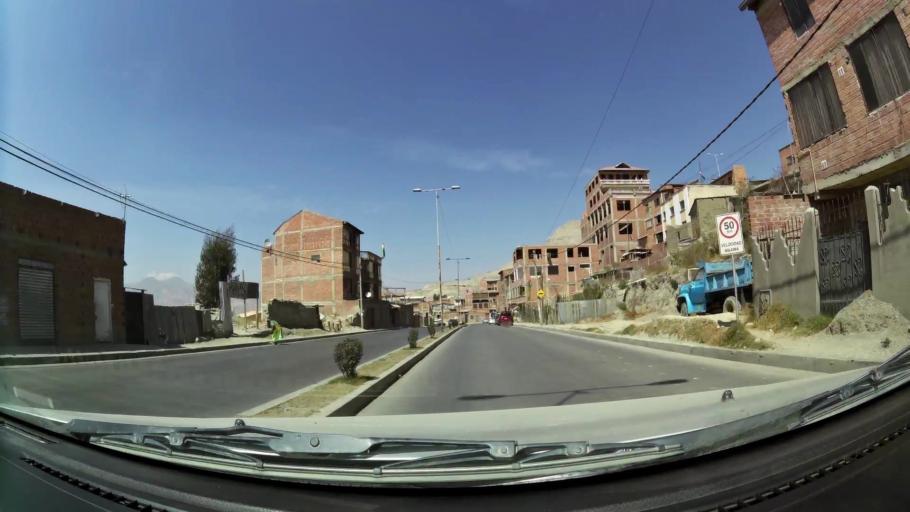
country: BO
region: La Paz
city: La Paz
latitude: -16.5274
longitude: -68.1250
